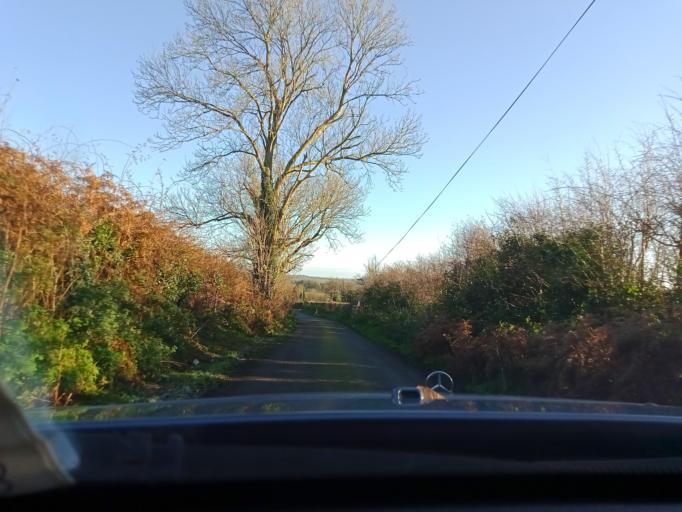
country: IE
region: Munster
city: Carrick-on-Suir
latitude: 52.4367
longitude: -7.4133
